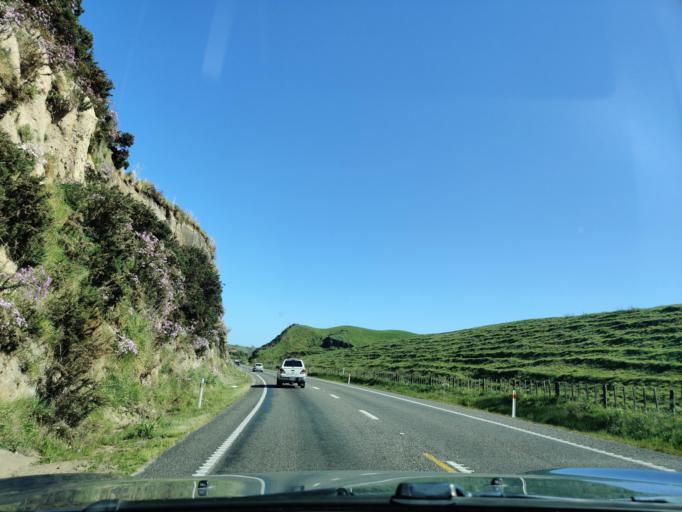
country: NZ
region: Manawatu-Wanganui
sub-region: Wanganui District
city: Wanganui
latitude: -40.0190
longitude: 175.1775
